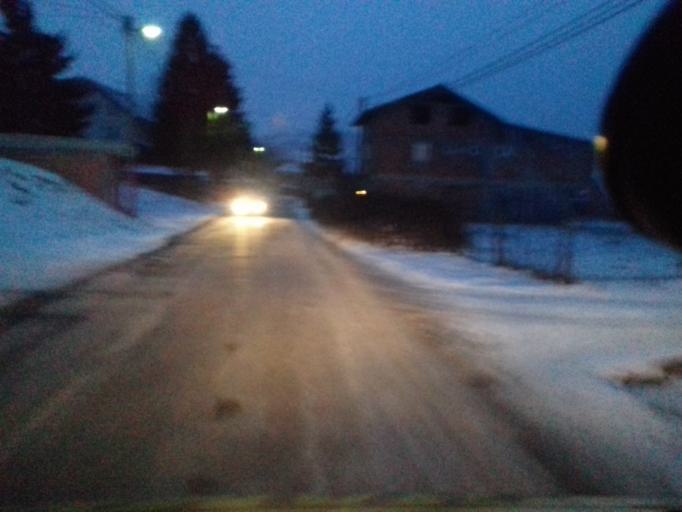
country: BA
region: Federation of Bosnia and Herzegovina
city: Vogosca
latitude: 43.8750
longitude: 18.3171
